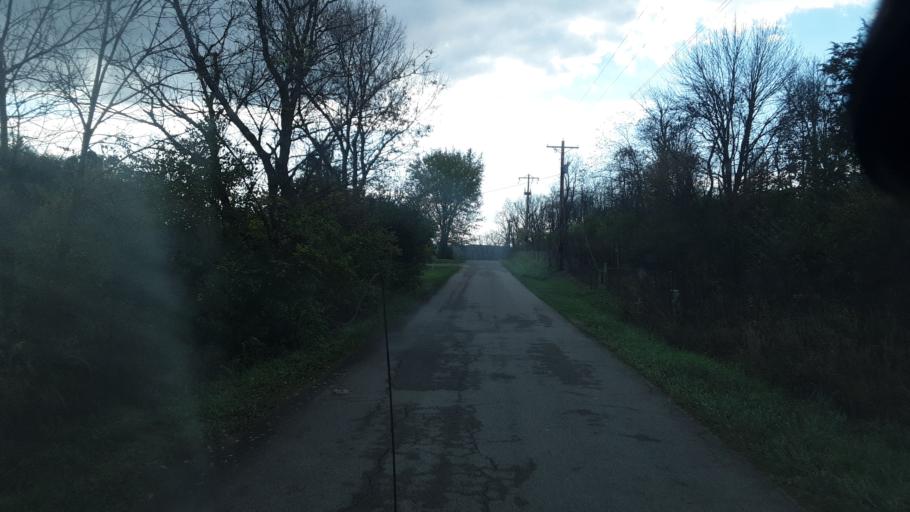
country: US
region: Ohio
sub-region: Highland County
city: Leesburg
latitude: 39.3364
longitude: -83.4739
